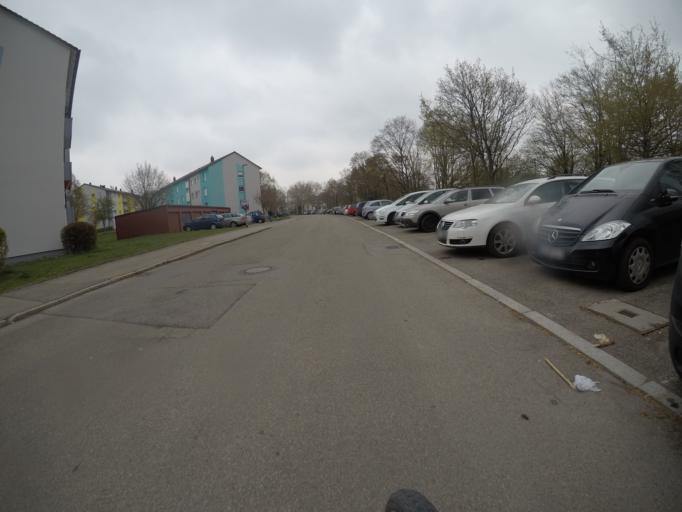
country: DE
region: Baden-Wuerttemberg
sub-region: Regierungsbezirk Stuttgart
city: Boeblingen
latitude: 48.6803
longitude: 8.9997
